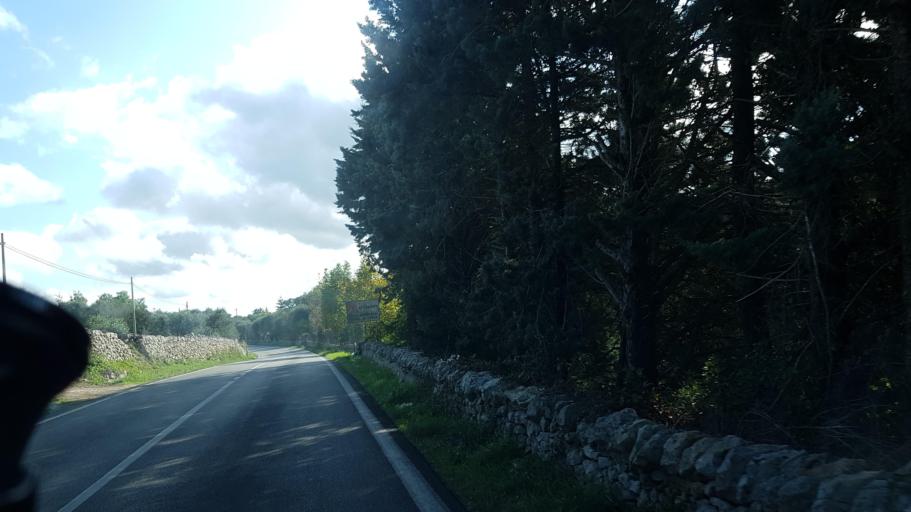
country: IT
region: Apulia
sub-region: Provincia di Brindisi
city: Ostuni
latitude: 40.6946
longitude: 17.5876
